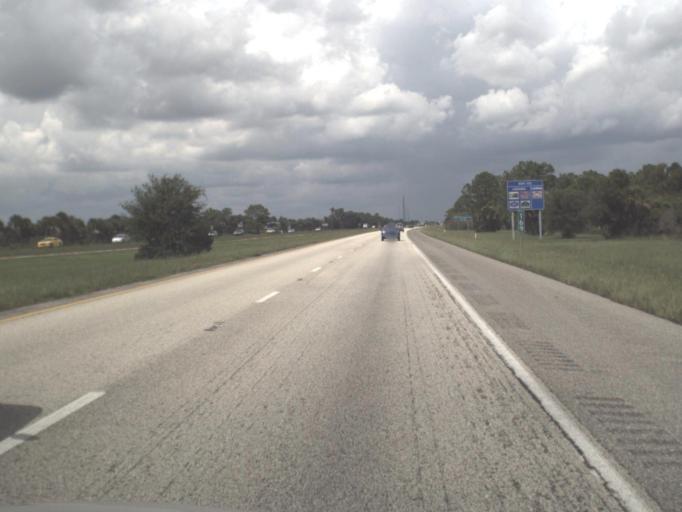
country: US
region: Florida
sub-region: Charlotte County
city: Harbour Heights
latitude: 27.0046
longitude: -82.0384
